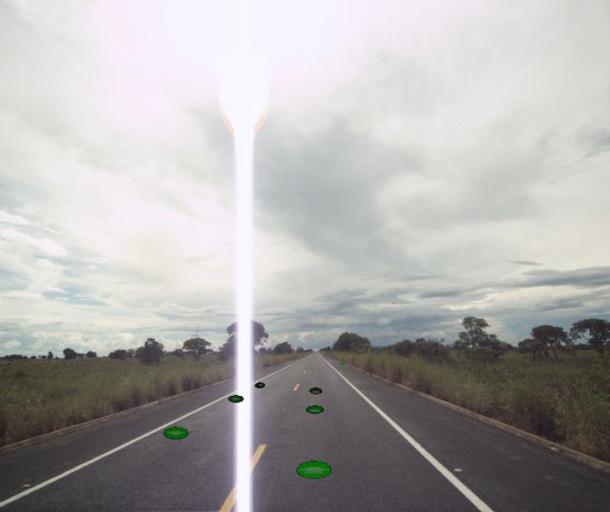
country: BR
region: Goias
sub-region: Sao Miguel Do Araguaia
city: Sao Miguel do Araguaia
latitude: -13.2808
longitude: -50.4951
